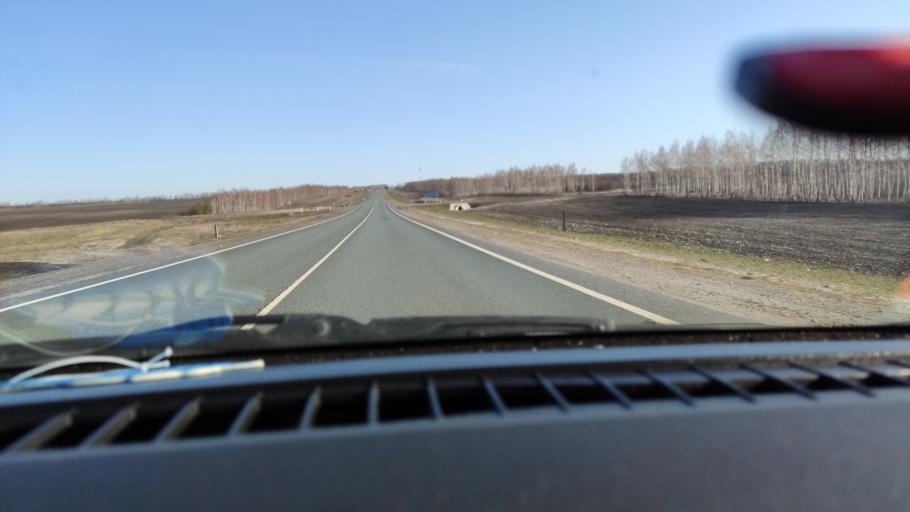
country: RU
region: Samara
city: Syzran'
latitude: 52.9138
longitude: 48.3005
